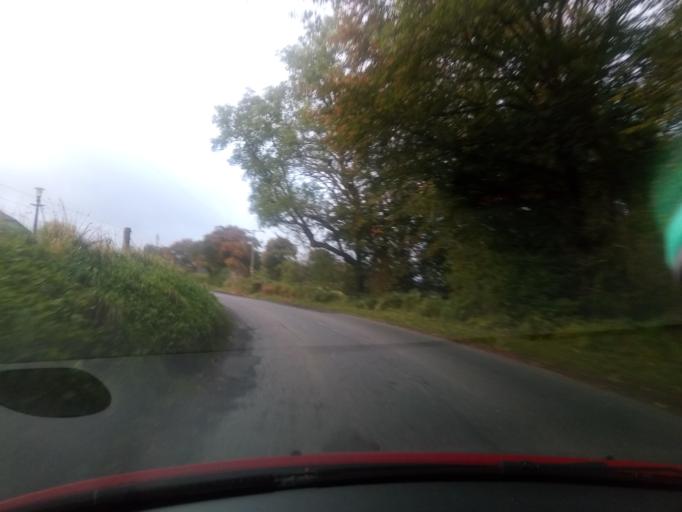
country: GB
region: Scotland
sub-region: The Scottish Borders
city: Hawick
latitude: 55.3457
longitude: -2.6489
